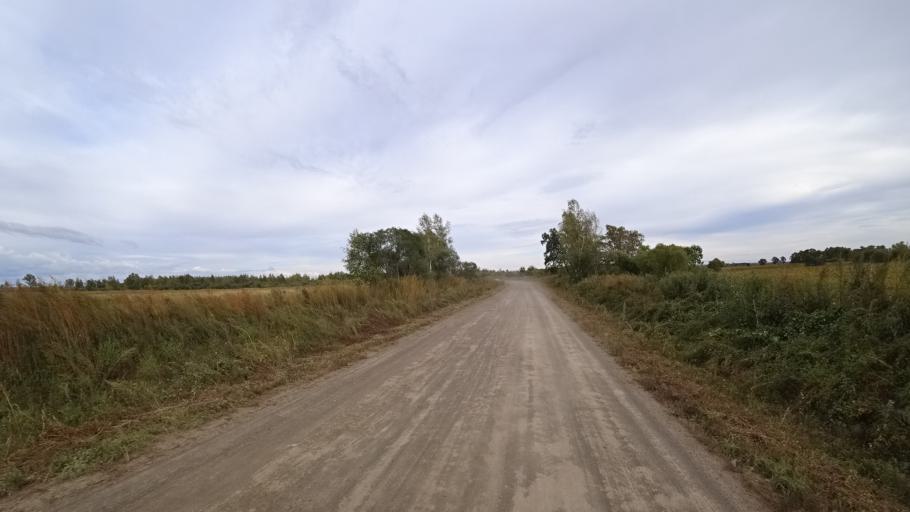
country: RU
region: Amur
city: Arkhara
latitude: 49.3534
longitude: 130.1439
